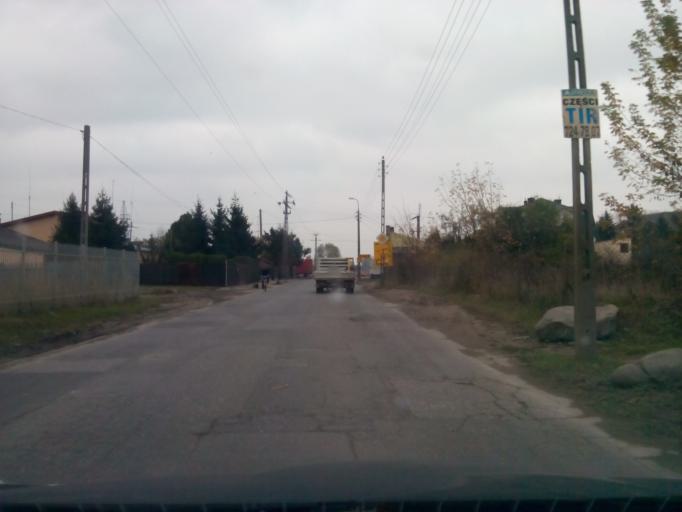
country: PL
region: Masovian Voivodeship
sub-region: Powiat pruszkowski
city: Pruszkow
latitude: 52.1738
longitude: 20.7709
